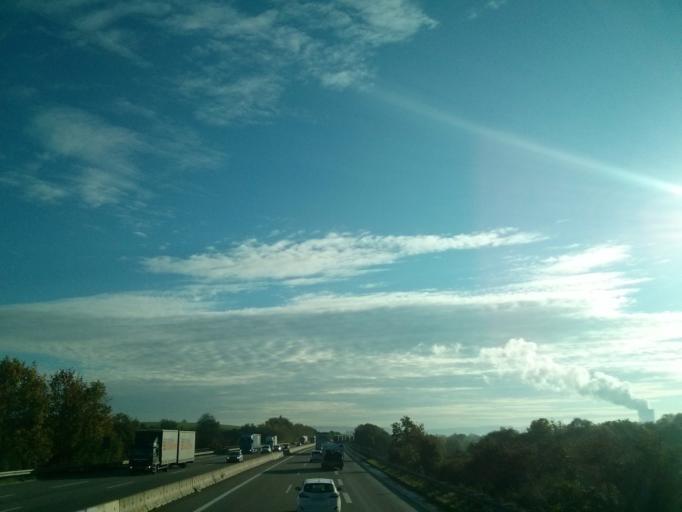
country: DE
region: Baden-Wuerttemberg
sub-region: Regierungsbezirk Stuttgart
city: Untereisesheim
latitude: 49.1889
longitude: 9.1668
